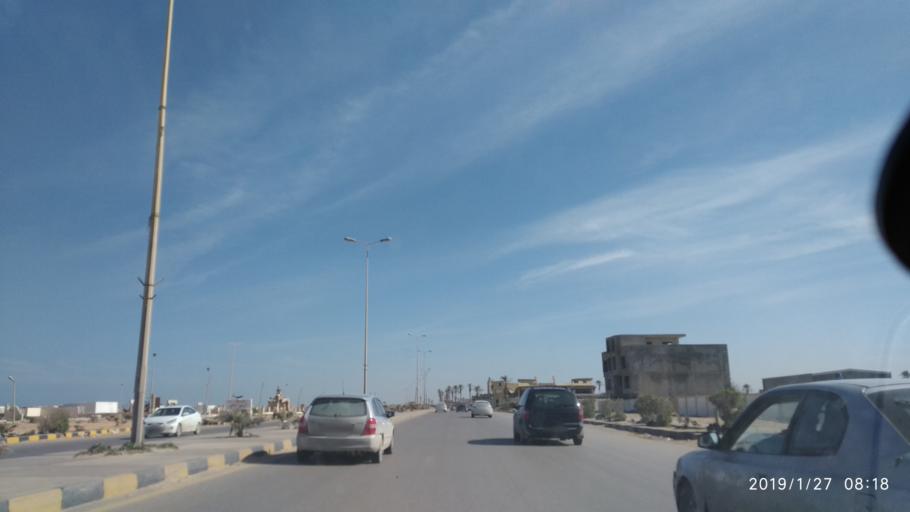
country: LY
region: Tripoli
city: Tagiura
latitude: 32.8952
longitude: 13.3301
